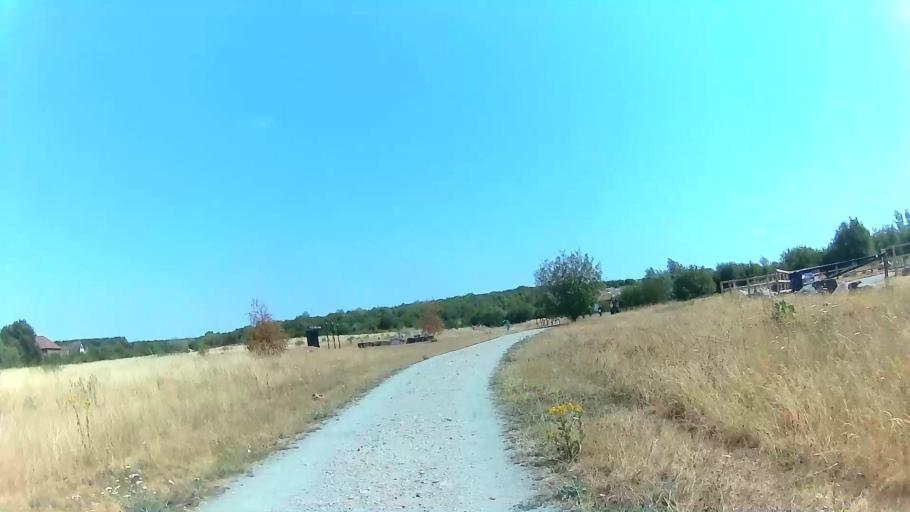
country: GB
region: England
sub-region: Greater London
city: Elm Park
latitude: 51.5261
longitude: 0.1931
